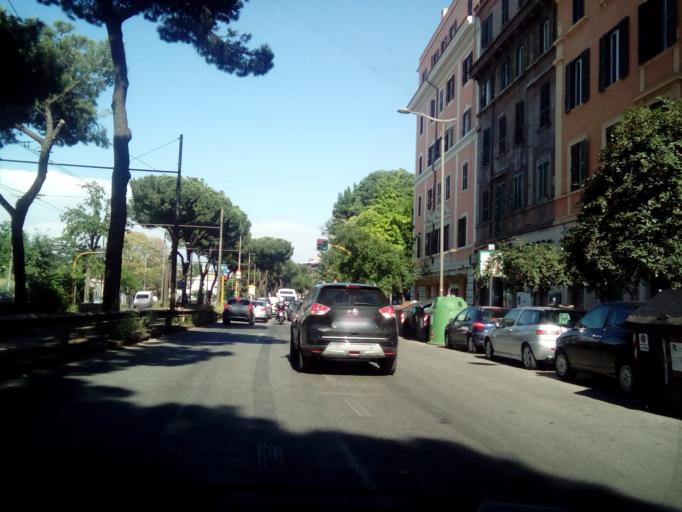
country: IT
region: Latium
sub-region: Citta metropolitana di Roma Capitale
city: Rome
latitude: 41.8924
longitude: 12.5352
